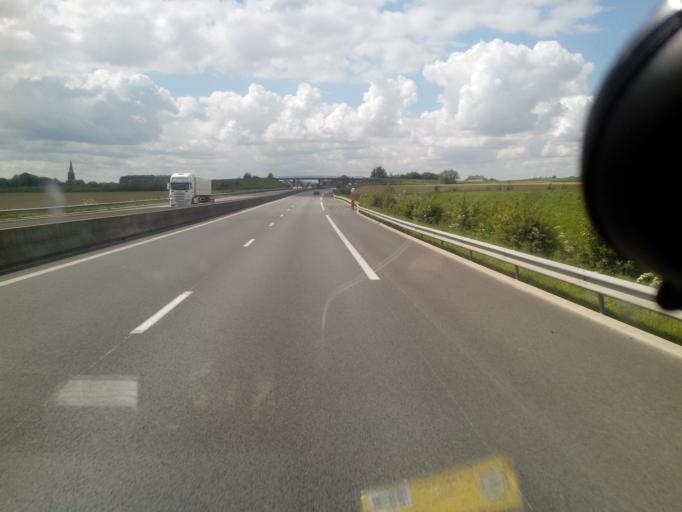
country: FR
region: Nord-Pas-de-Calais
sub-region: Departement du Nord
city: Godewaersvelde
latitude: 50.7527
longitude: 2.6590
